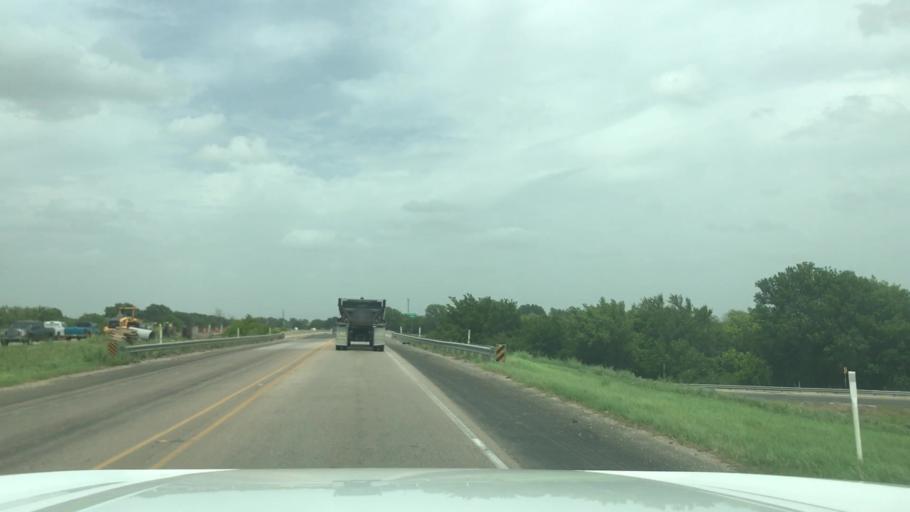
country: US
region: Texas
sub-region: McLennan County
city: Beverly
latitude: 31.5342
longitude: -97.0752
